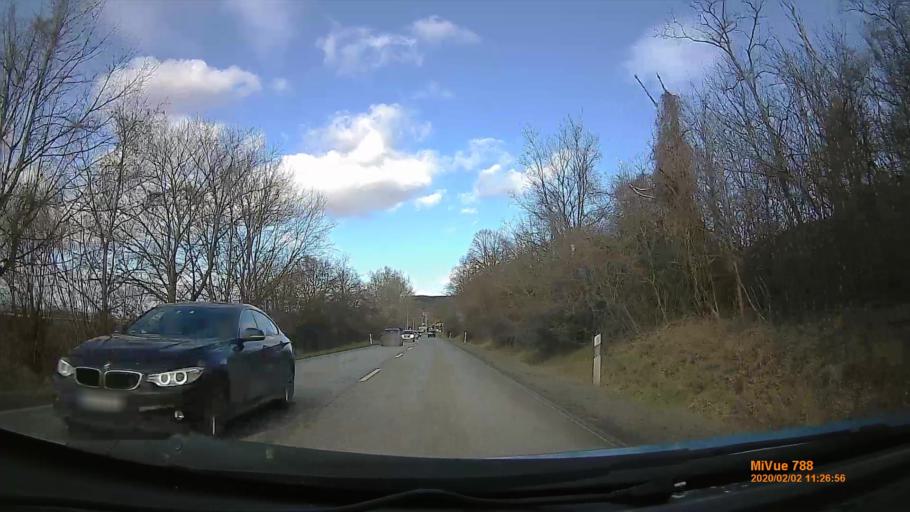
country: HU
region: Gyor-Moson-Sopron
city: Sopron
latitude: 47.7121
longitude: 16.5730
